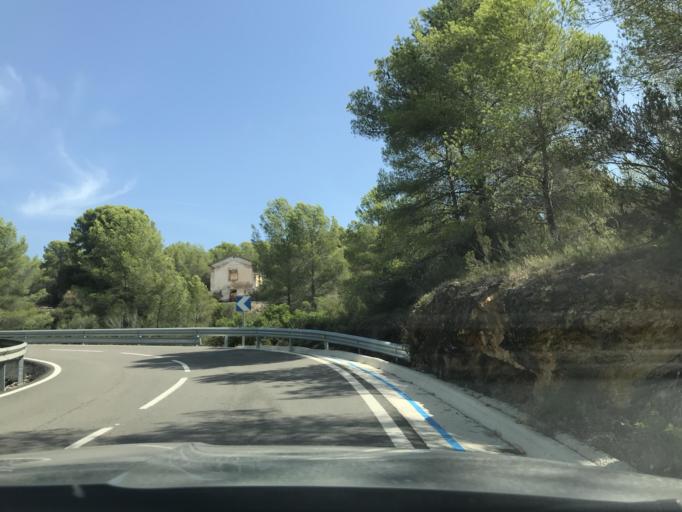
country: ES
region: Catalonia
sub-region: Provincia de Tarragona
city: Salomo
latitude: 41.1908
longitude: 1.3837
